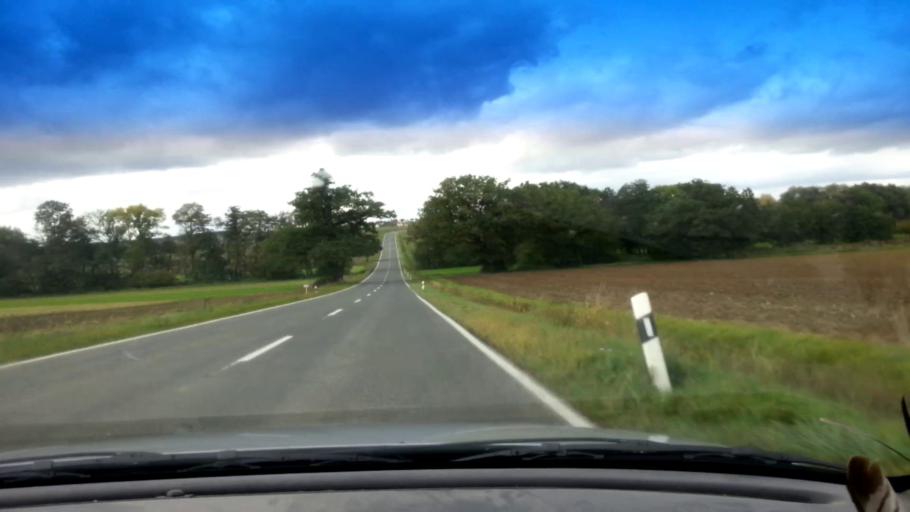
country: DE
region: Bavaria
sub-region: Upper Franconia
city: Schesslitz
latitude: 49.9858
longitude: 11.0136
